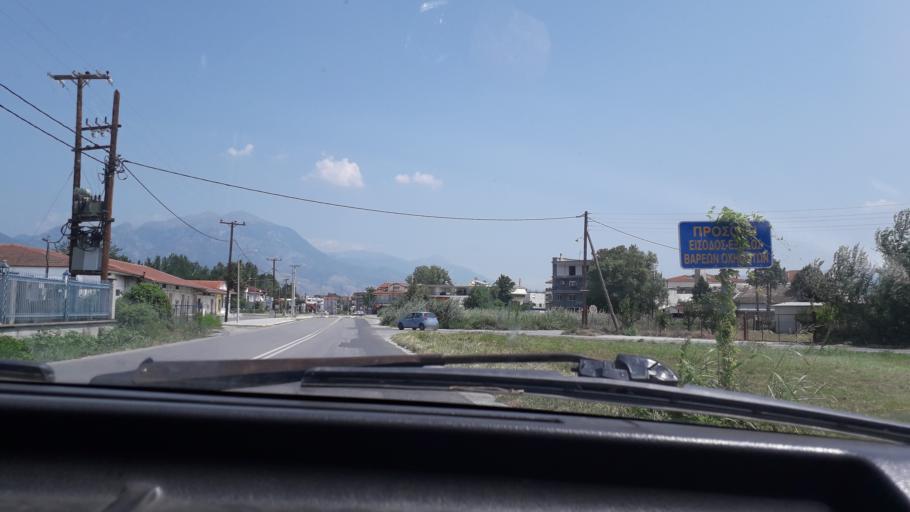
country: GR
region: Central Macedonia
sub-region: Nomos Pellis
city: Aridaia
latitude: 40.9680
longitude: 22.0549
